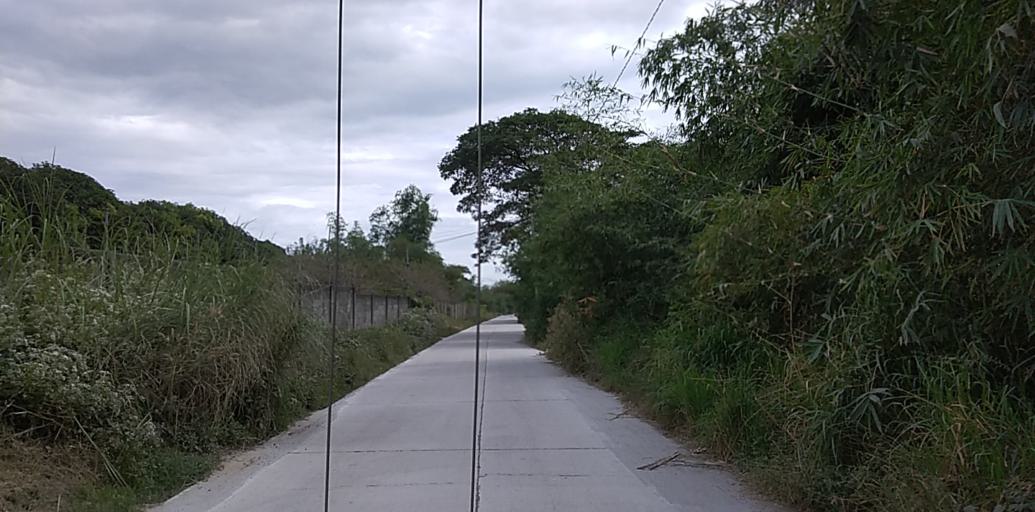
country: PH
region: Central Luzon
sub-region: Province of Pampanga
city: Pulung Santol
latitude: 15.0581
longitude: 120.5561
